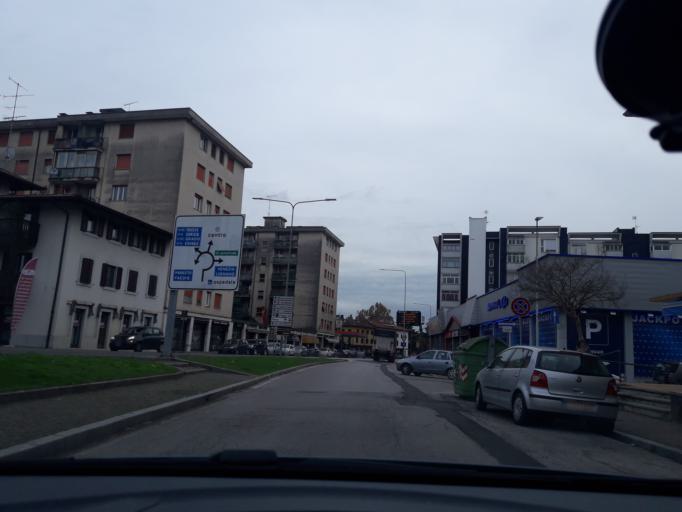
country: IT
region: Friuli Venezia Giulia
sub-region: Provincia di Udine
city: Udine
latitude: 46.0803
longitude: 13.2340
